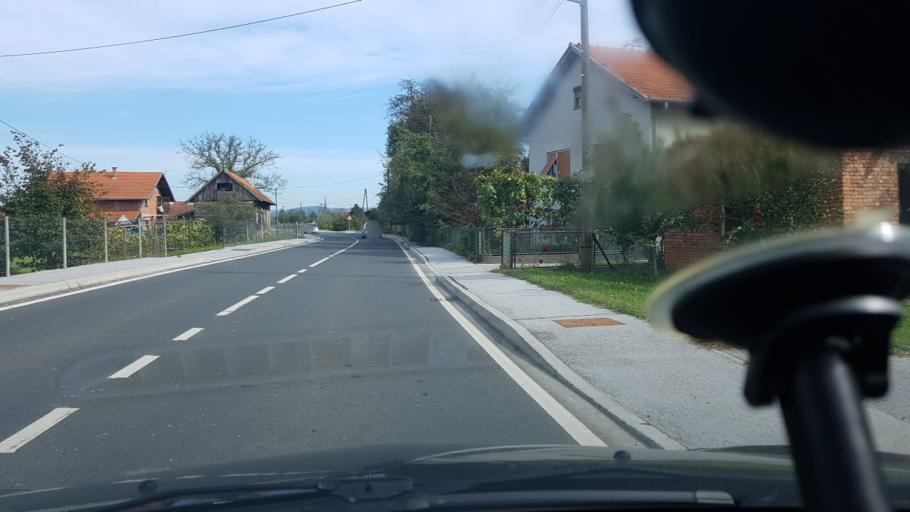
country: HR
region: Krapinsko-Zagorska
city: Marija Bistrica
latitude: 46.0613
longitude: 16.1855
